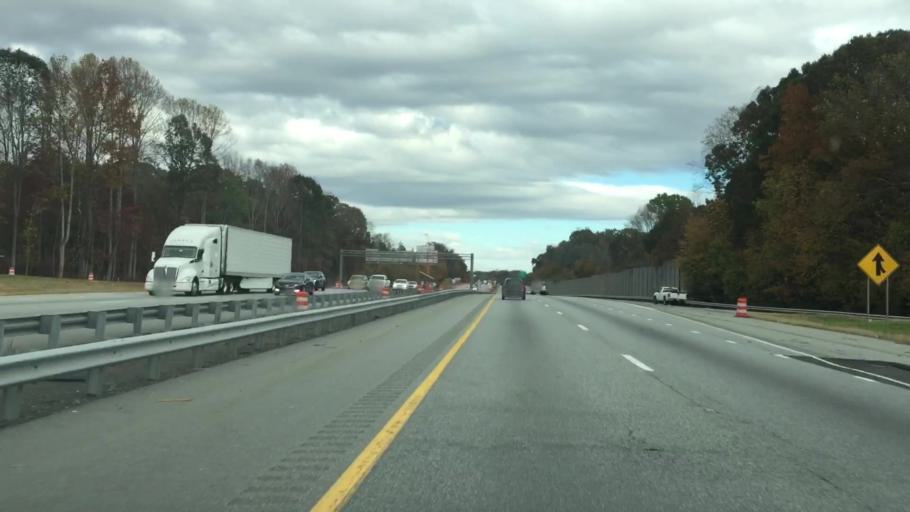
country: US
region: North Carolina
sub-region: Forsyth County
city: Clemmons
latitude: 36.0234
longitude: -80.4041
